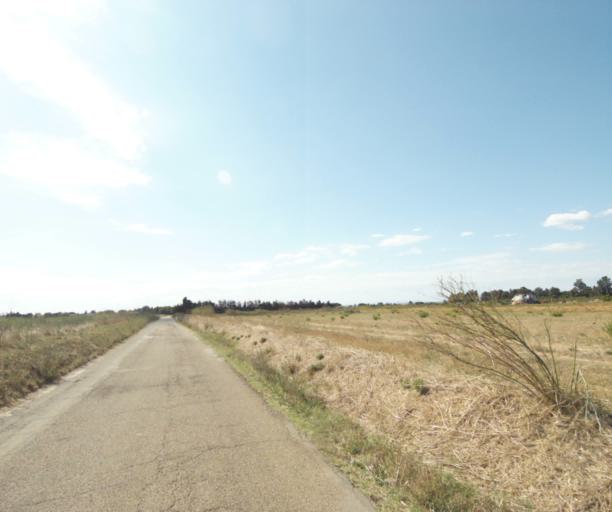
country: FR
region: Languedoc-Roussillon
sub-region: Departement du Gard
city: Bouillargues
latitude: 43.8001
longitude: 4.4461
